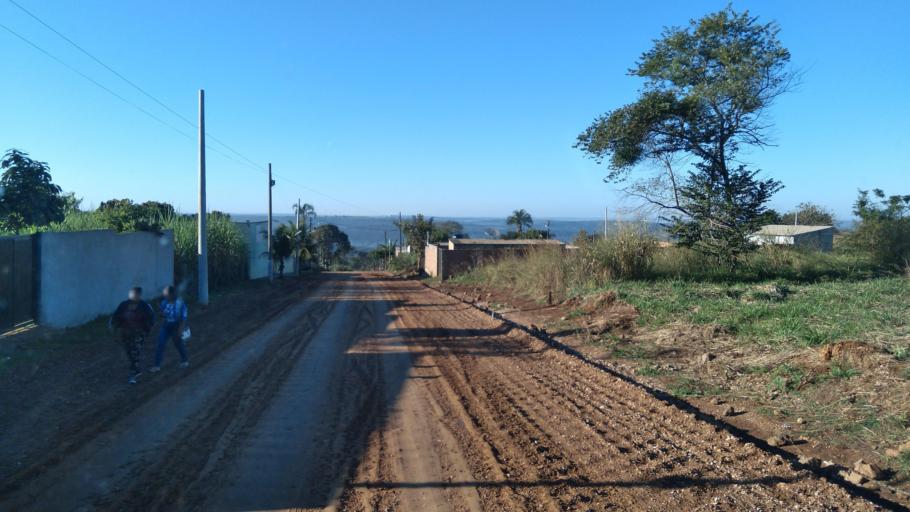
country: BR
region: Goias
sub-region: Mineiros
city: Mineiros
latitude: -17.5865
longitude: -52.5496
